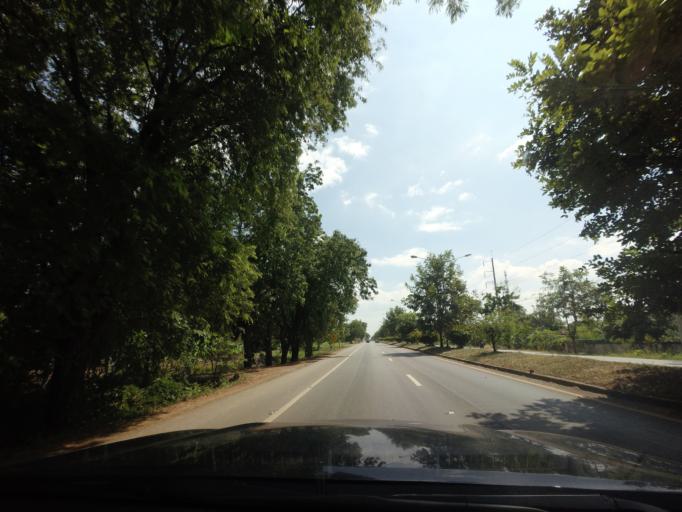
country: TH
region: Phetchabun
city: Nong Phai
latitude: 15.9184
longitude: 101.0262
